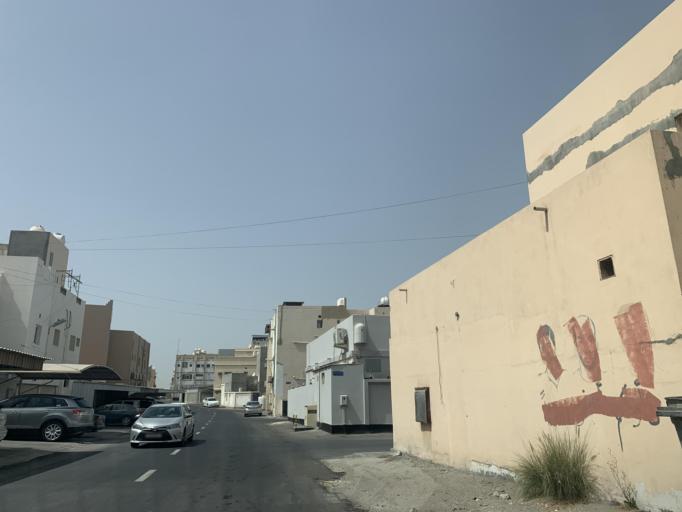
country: BH
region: Northern
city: Madinat `Isa
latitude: 26.1554
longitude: 50.5171
